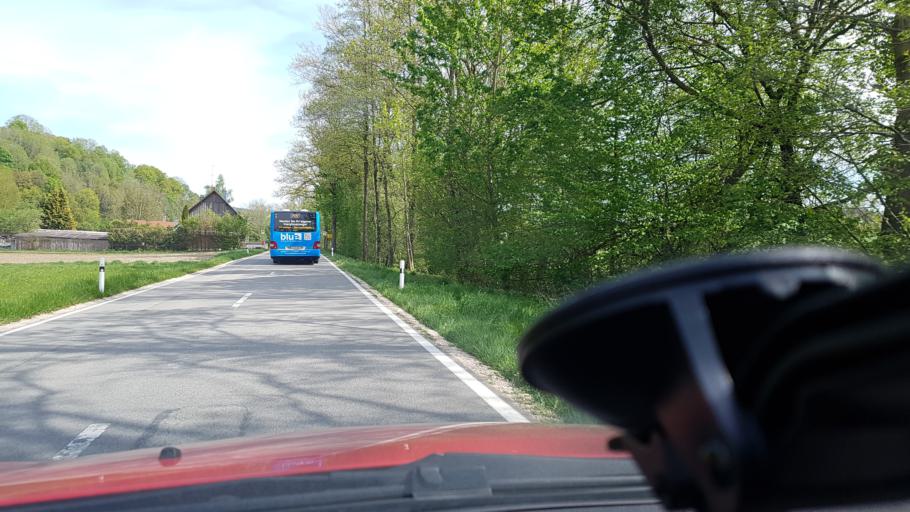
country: DE
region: Bavaria
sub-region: Lower Bavaria
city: Stubenberg
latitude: 48.3291
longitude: 13.1117
